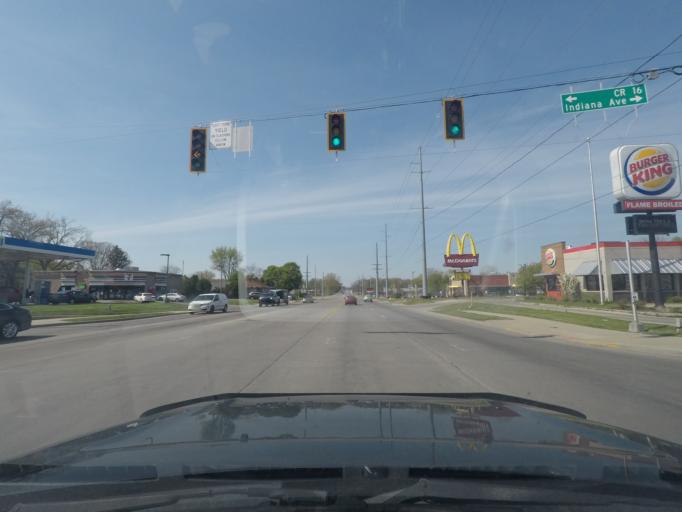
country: US
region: Indiana
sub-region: Elkhart County
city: Elkhart
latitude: 41.6744
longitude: -86.0032
